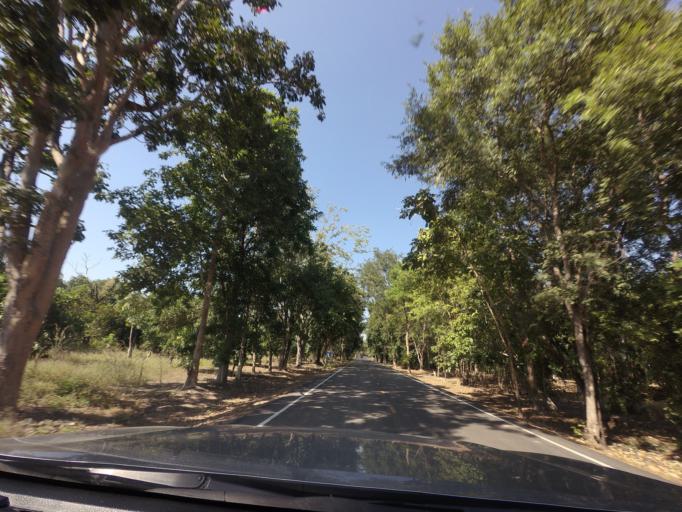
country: TH
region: Sukhothai
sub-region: Amphoe Si Satchanalai
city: Si Satchanalai
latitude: 17.4228
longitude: 99.7889
